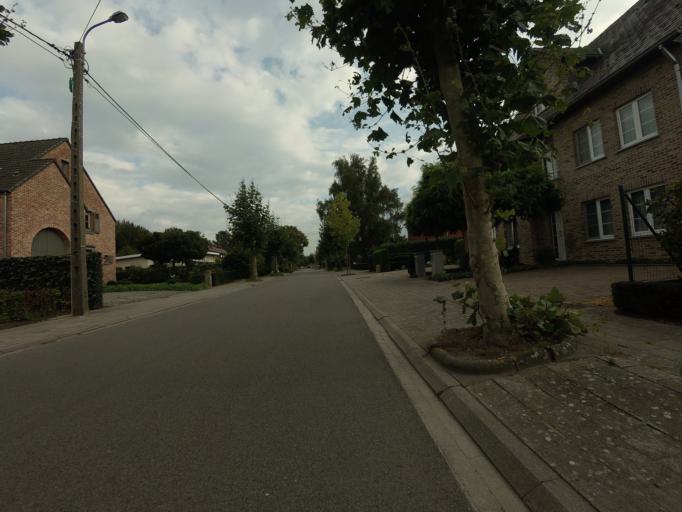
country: BE
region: Flanders
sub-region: Provincie Vlaams-Brabant
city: Kapelle-op-den-Bos
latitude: 51.0149
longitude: 4.3405
